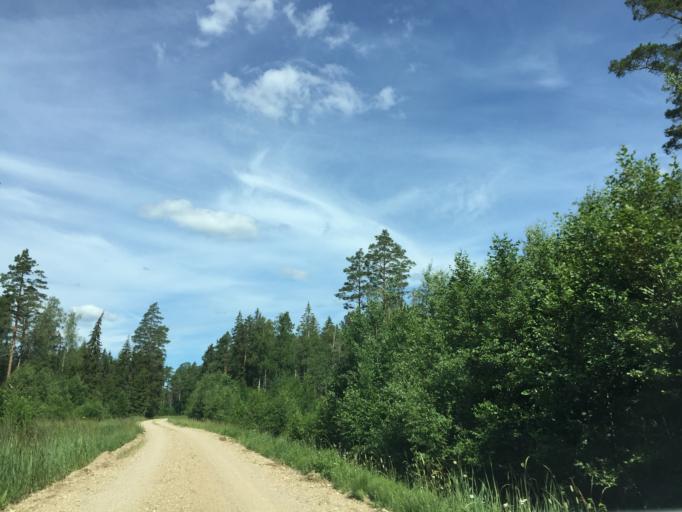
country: LV
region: Dundaga
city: Dundaga
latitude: 57.4243
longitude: 22.0771
